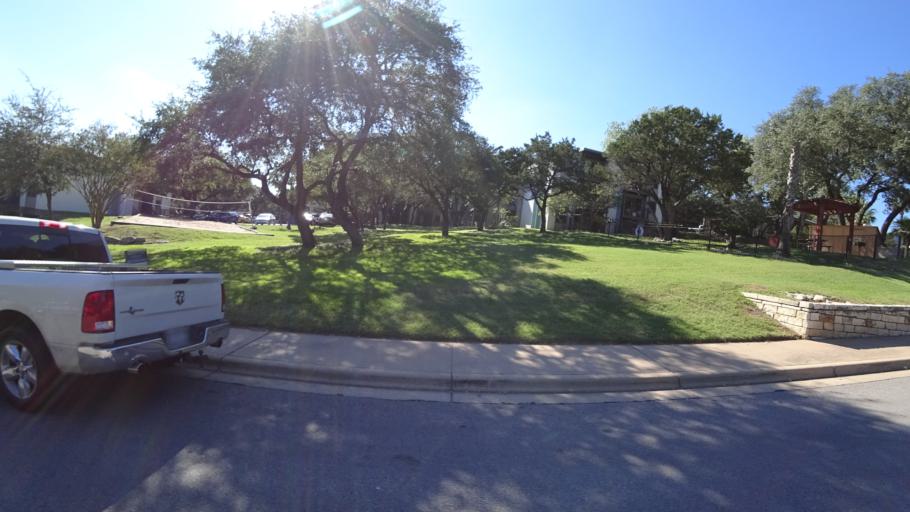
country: US
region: Texas
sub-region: Travis County
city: Rollingwood
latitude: 30.2607
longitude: -97.7864
